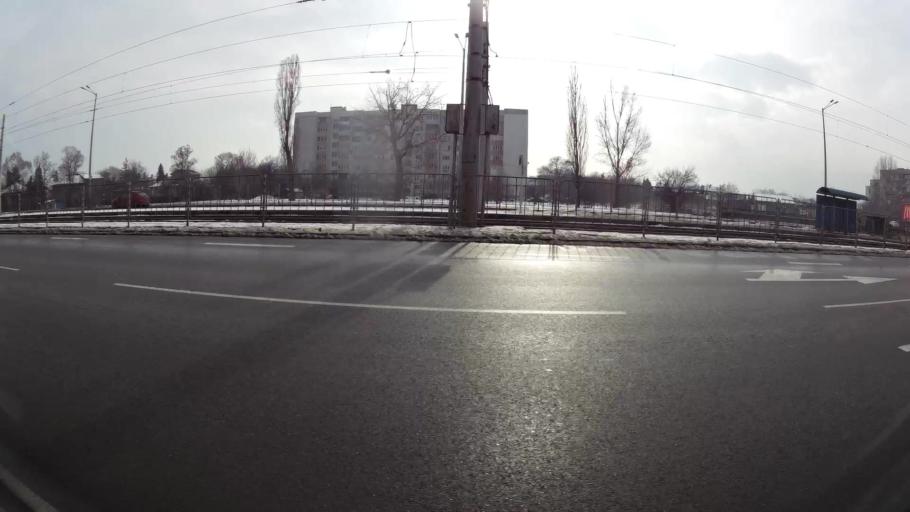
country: BG
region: Sofia-Capital
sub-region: Stolichna Obshtina
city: Sofia
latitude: 42.7010
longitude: 23.3744
